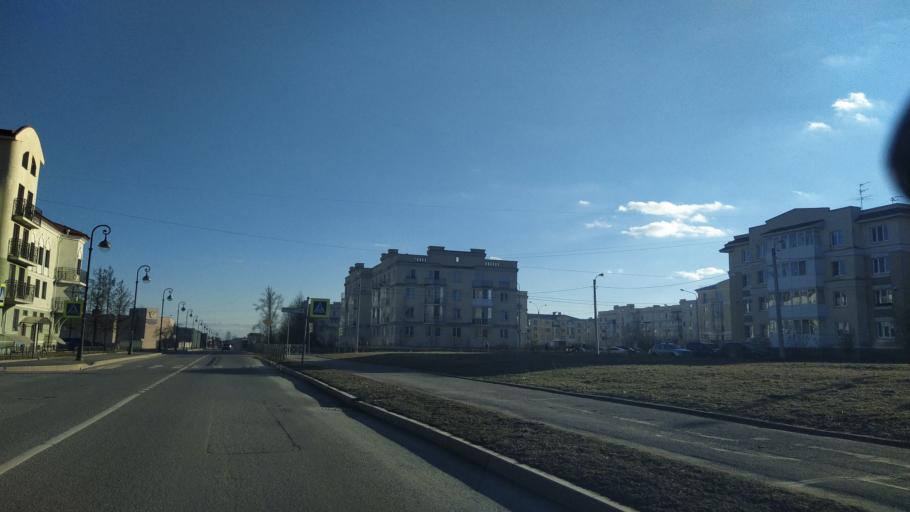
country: RU
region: St.-Petersburg
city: Pushkin
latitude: 59.7041
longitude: 30.3923
